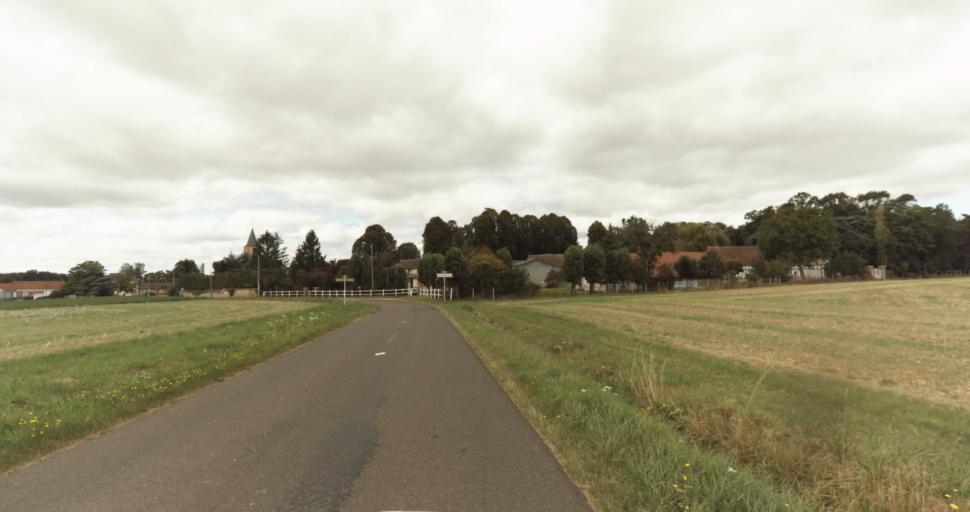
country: FR
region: Haute-Normandie
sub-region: Departement de l'Eure
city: Evreux
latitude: 48.9361
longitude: 1.2035
